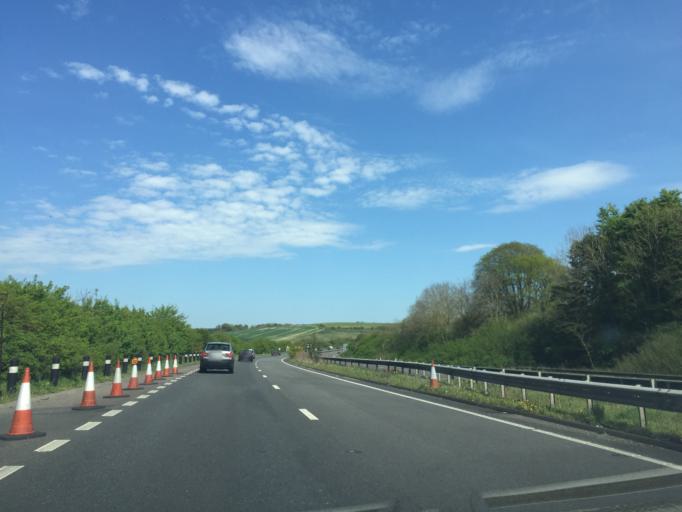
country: GB
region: England
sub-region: Kent
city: Hawkinge
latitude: 51.1115
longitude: 1.1854
